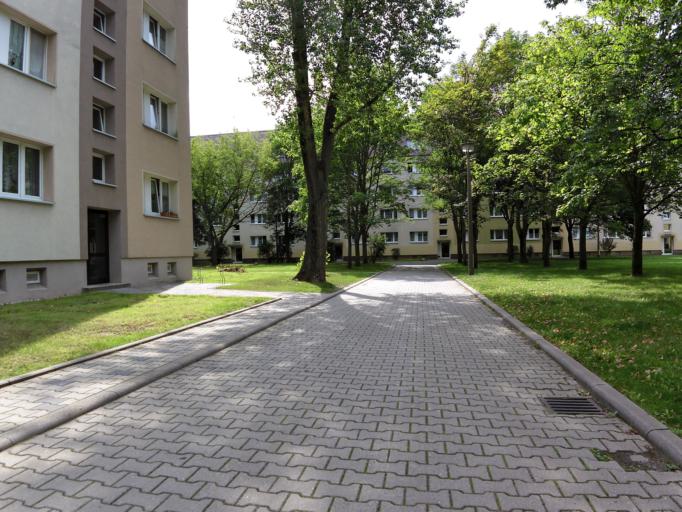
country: DE
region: Saxony
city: Rackwitz
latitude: 51.3830
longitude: 12.4189
